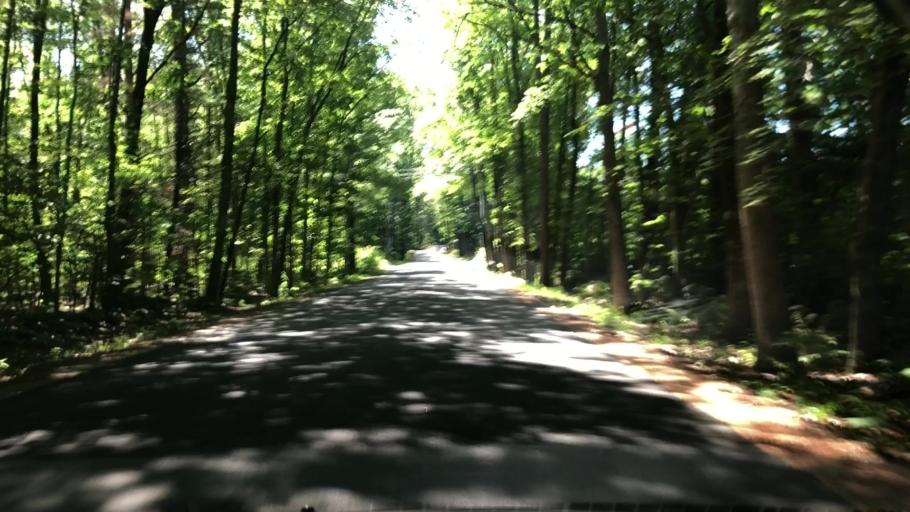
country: US
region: New Hampshire
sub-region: Hillsborough County
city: Milford
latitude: 42.8584
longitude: -71.5806
